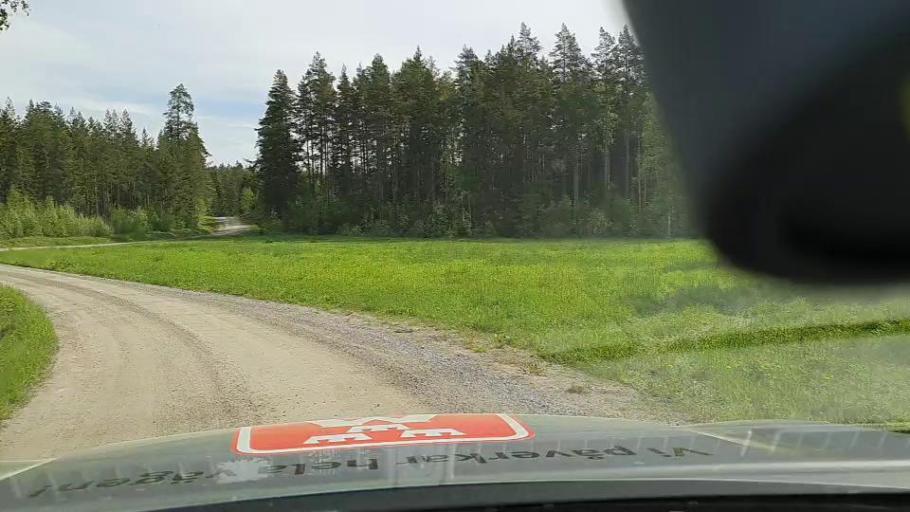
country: SE
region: Soedermanland
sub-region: Flens Kommun
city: Malmkoping
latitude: 59.2603
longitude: 16.8747
